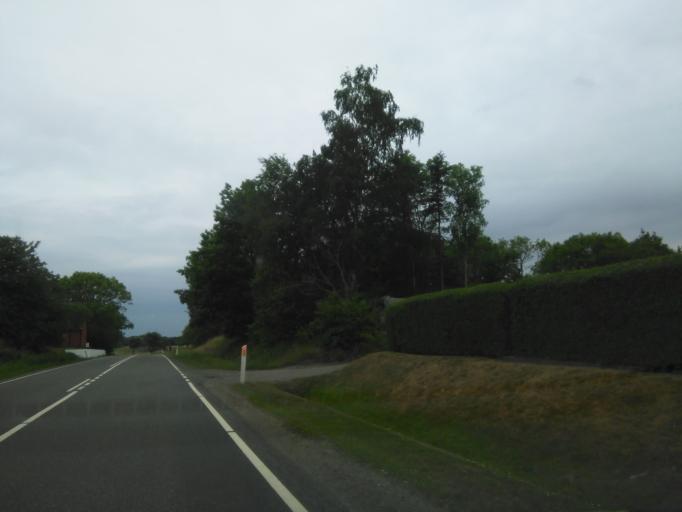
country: DK
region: Capital Region
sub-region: Bornholm Kommune
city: Akirkeby
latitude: 55.0895
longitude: 14.8771
